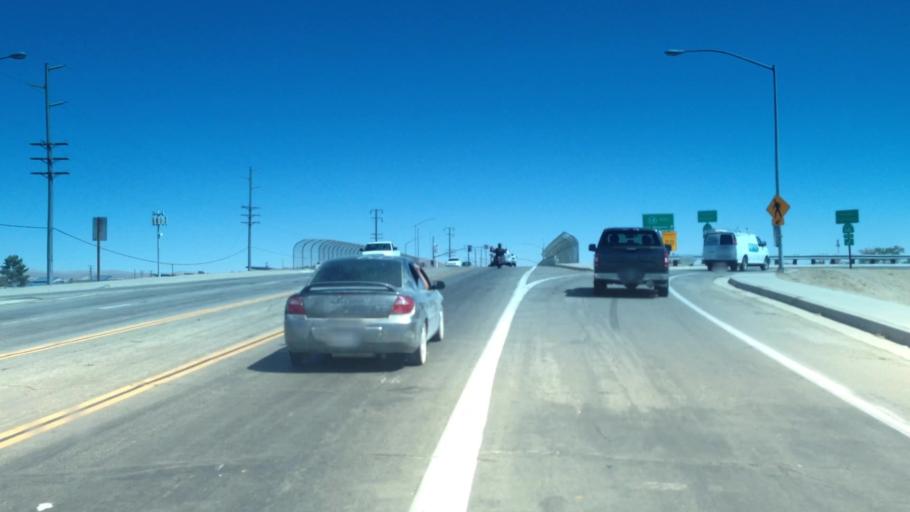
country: US
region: California
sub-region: Kern County
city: Rosamond
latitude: 34.8642
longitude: -118.1730
